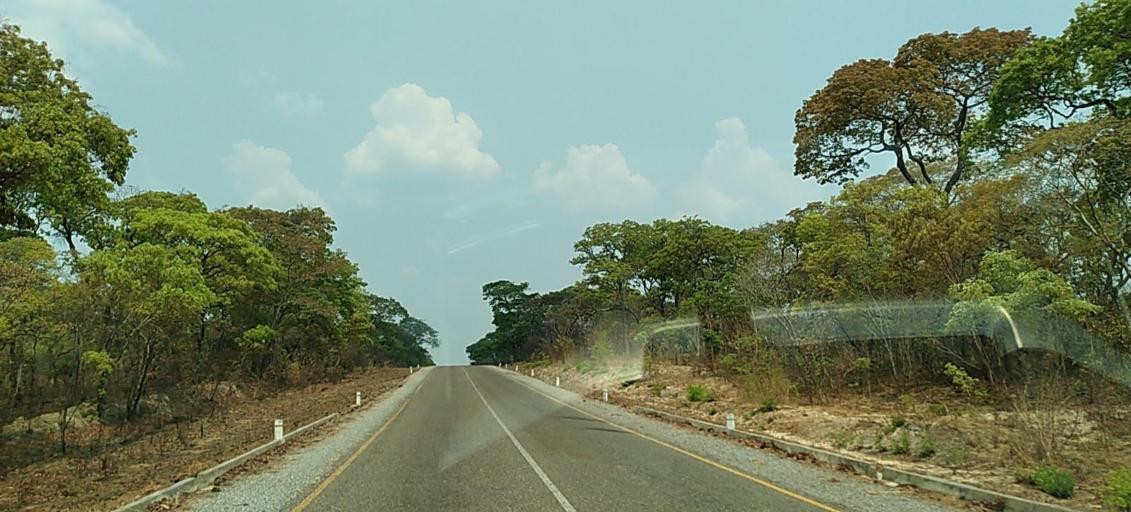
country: ZM
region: North-Western
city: Zambezi
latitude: -13.5682
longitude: 23.2259
